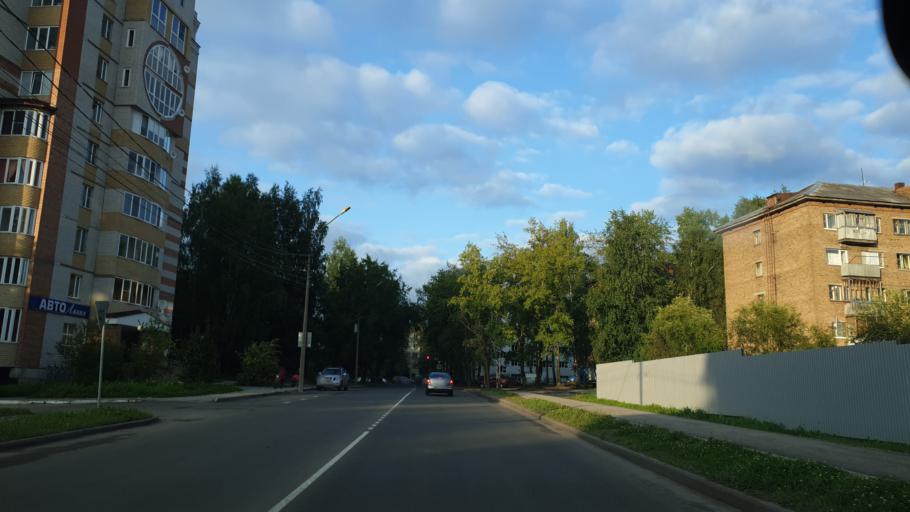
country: RU
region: Komi Republic
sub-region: Syktyvdinskiy Rayon
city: Syktyvkar
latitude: 61.6665
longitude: 50.8096
